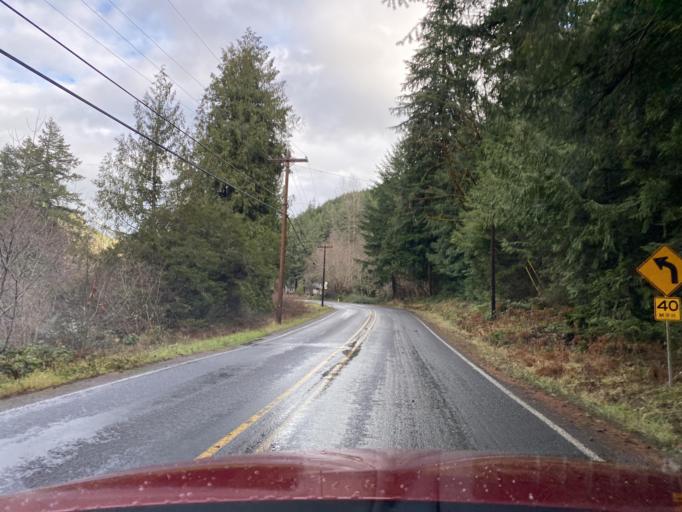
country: US
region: Oregon
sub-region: Lane County
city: Oakridge
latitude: 43.7564
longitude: -122.5090
